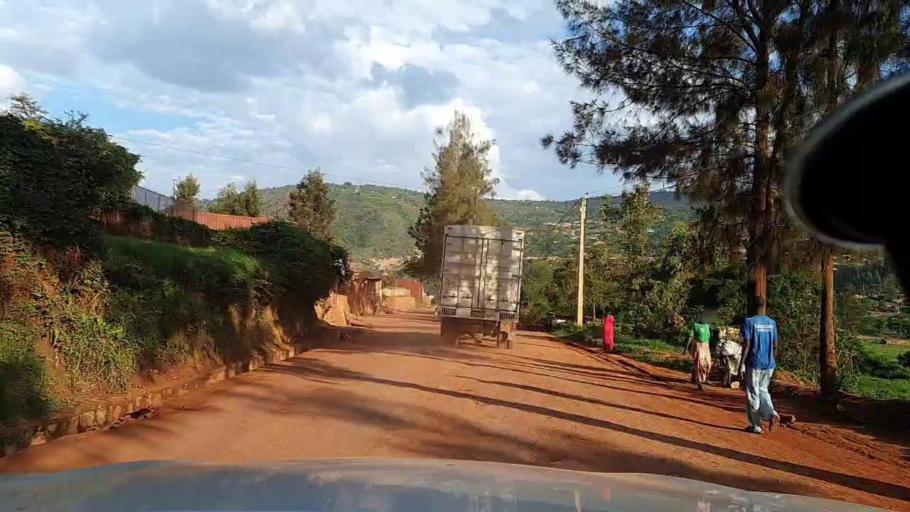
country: RW
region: Kigali
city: Kigali
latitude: -1.9470
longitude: 30.0162
